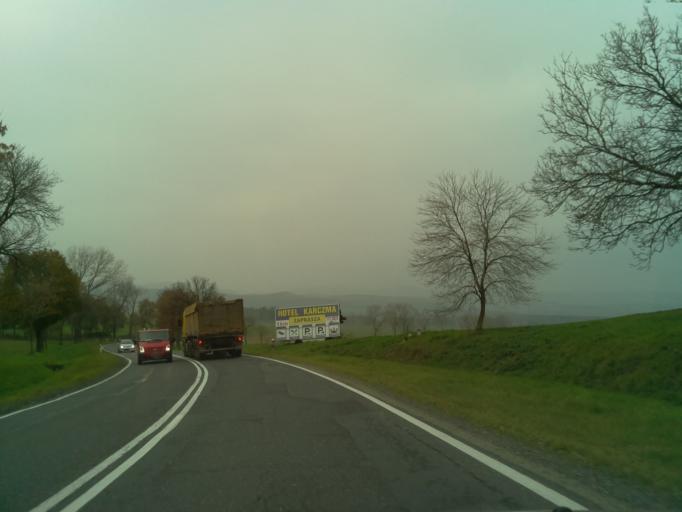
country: PL
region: Lower Silesian Voivodeship
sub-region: Powiat walbrzyski
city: Stare Bogaczowice
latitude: 50.9142
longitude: 16.1889
